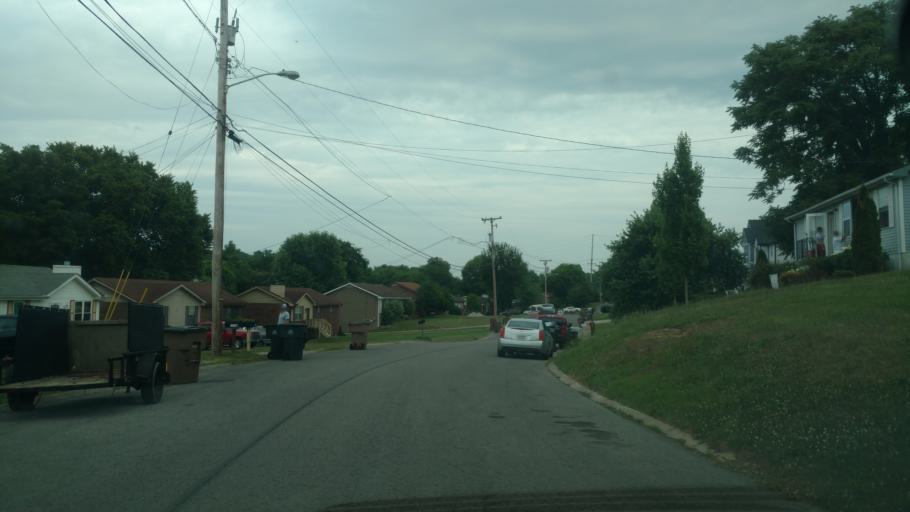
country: US
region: Tennessee
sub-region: Davidson County
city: Nashville
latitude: 36.1896
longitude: -86.7120
